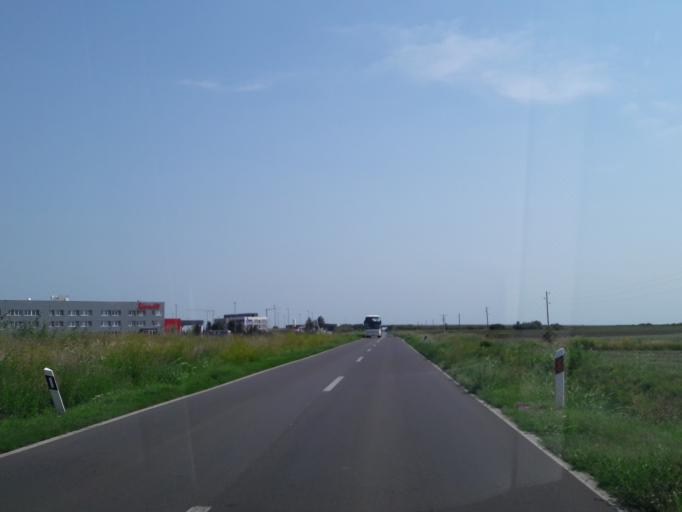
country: HR
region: Osjecko-Baranjska
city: Tenja
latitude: 45.5312
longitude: 18.7723
